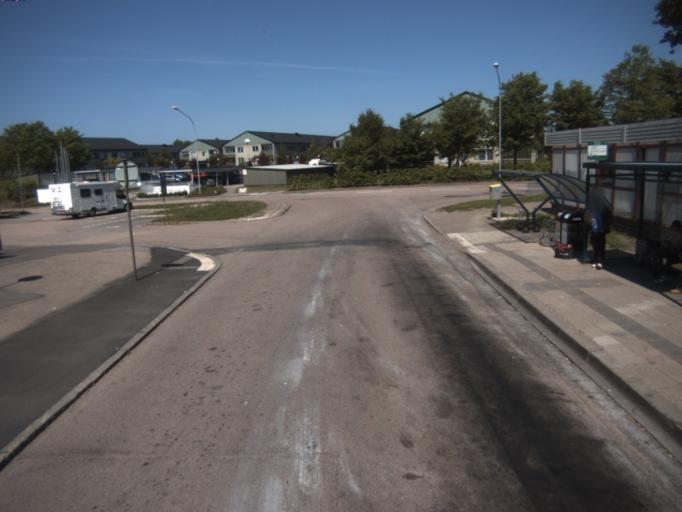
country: SE
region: Skane
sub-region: Helsingborg
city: Rydeback
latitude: 56.0122
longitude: 12.7611
